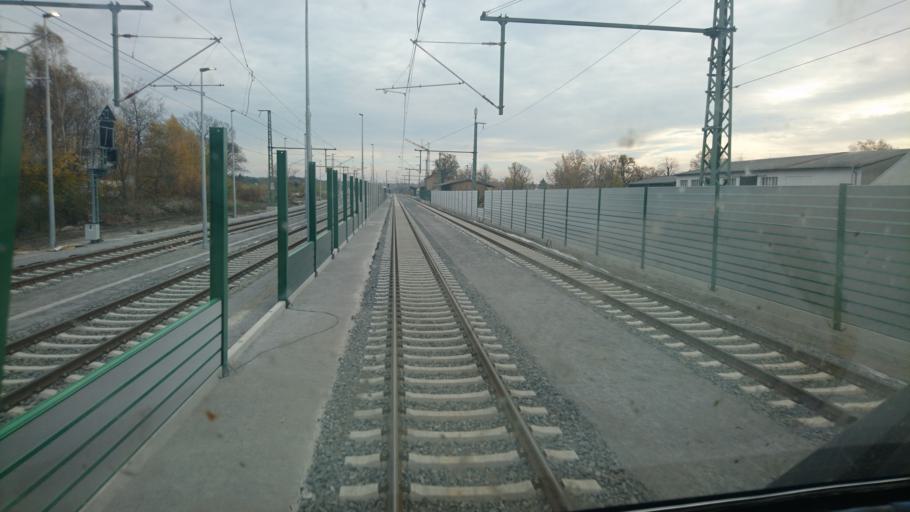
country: DE
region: Saxony
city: Niesky
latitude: 51.2992
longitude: 14.8280
